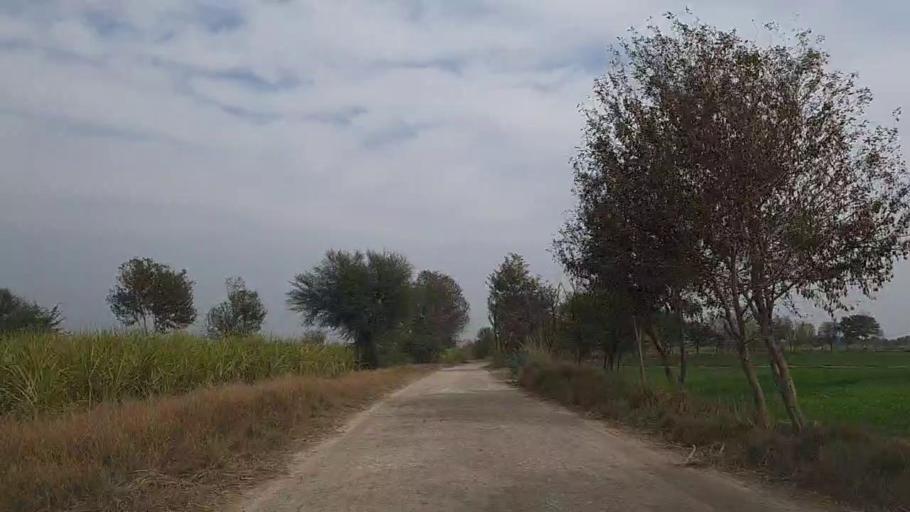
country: PK
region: Sindh
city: Daur
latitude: 26.4238
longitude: 68.4571
